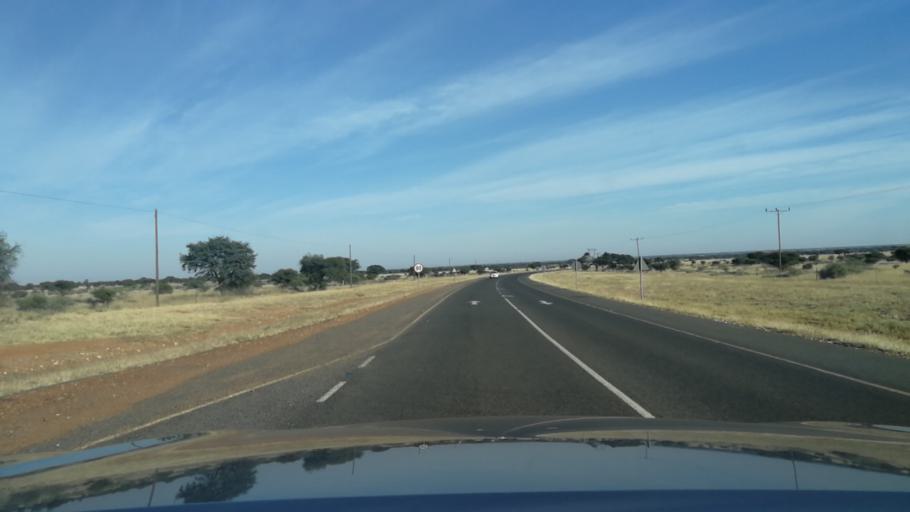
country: BW
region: South East
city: Janeng
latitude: -25.4787
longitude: 25.5072
